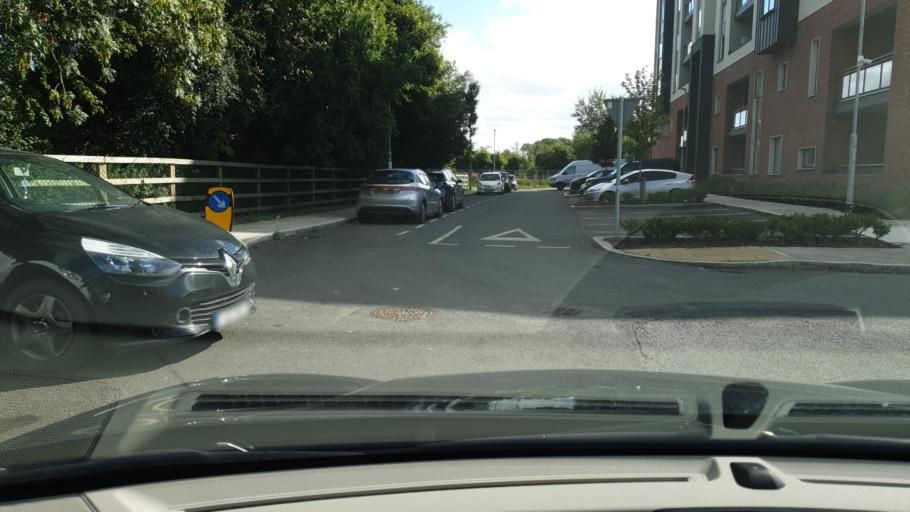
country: IE
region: Leinster
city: Hartstown
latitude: 53.3863
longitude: -6.4343
